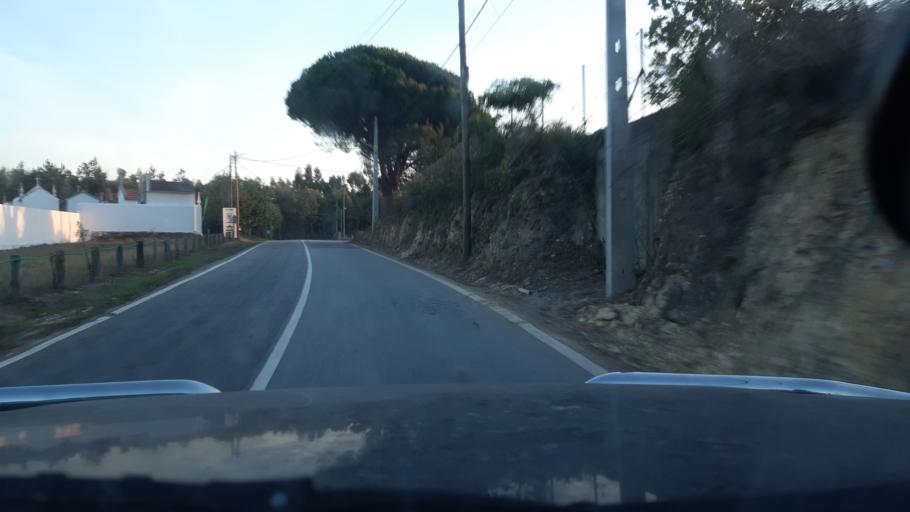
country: PT
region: Aveiro
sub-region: Agueda
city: Aguada de Cima
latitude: 40.5688
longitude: -8.3680
